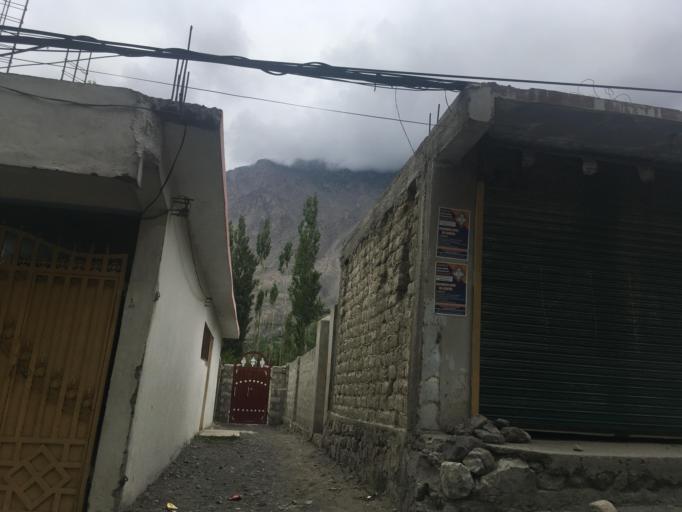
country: PK
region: Gilgit-Baltistan
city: Skardu
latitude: 35.2773
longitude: 75.6372
